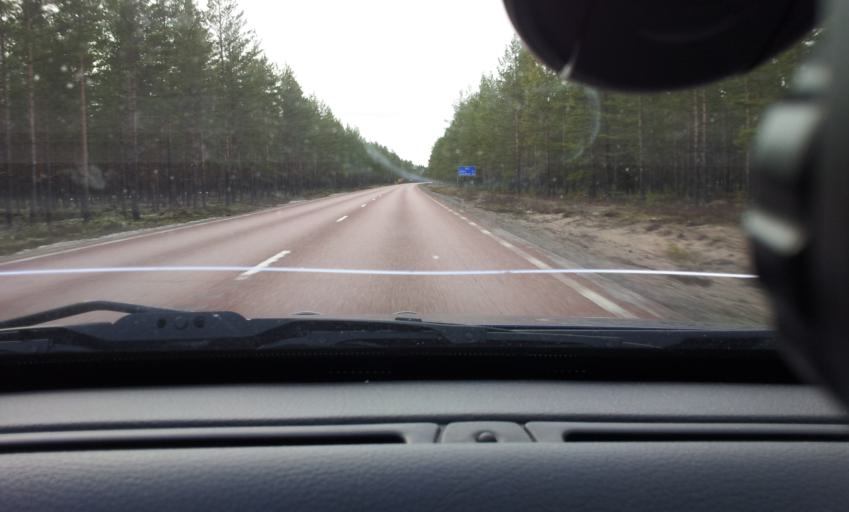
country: SE
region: Gaevleborg
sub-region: Ljusdals Kommun
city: Farila
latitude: 61.8907
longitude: 15.6670
